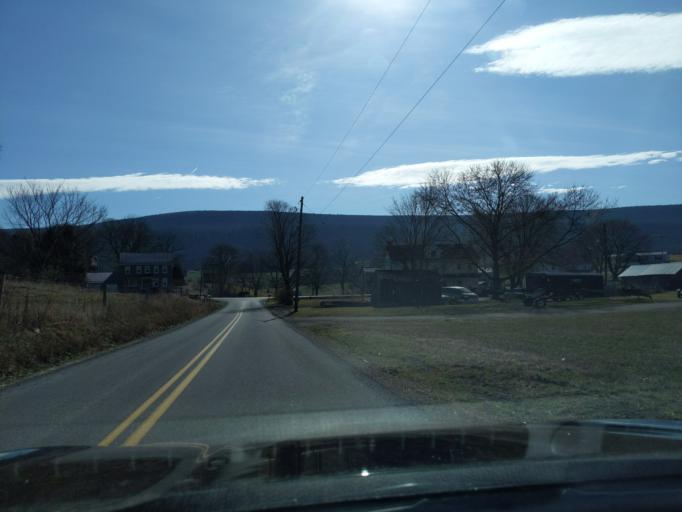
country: US
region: Pennsylvania
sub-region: Blair County
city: Williamsburg
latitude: 40.3743
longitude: -78.2378
